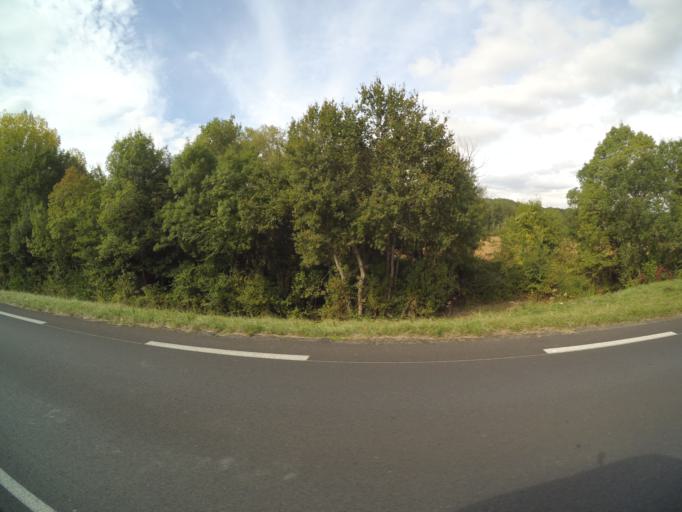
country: FR
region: Centre
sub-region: Departement d'Indre-et-Loire
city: Langeais
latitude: 47.2997
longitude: 0.3469
